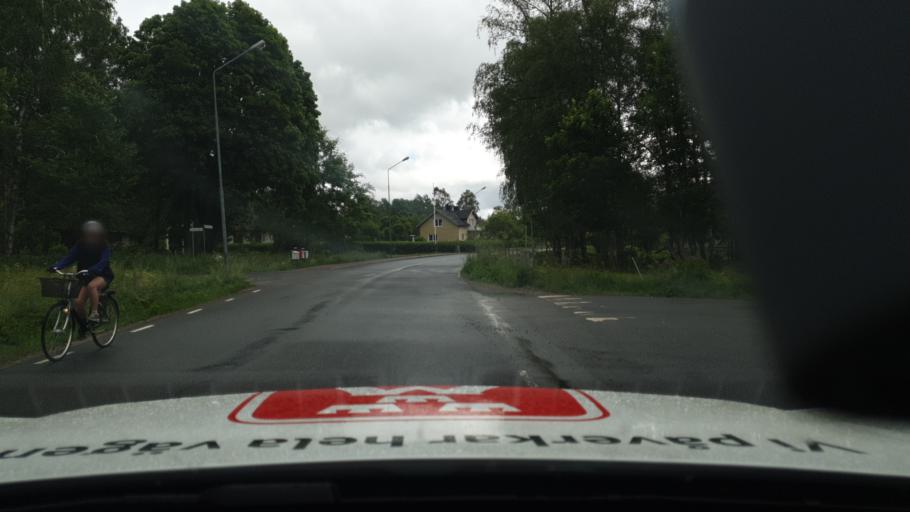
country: SE
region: Joenkoeping
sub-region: Mullsjo Kommun
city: Mullsjoe
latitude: 57.9896
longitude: 13.7538
